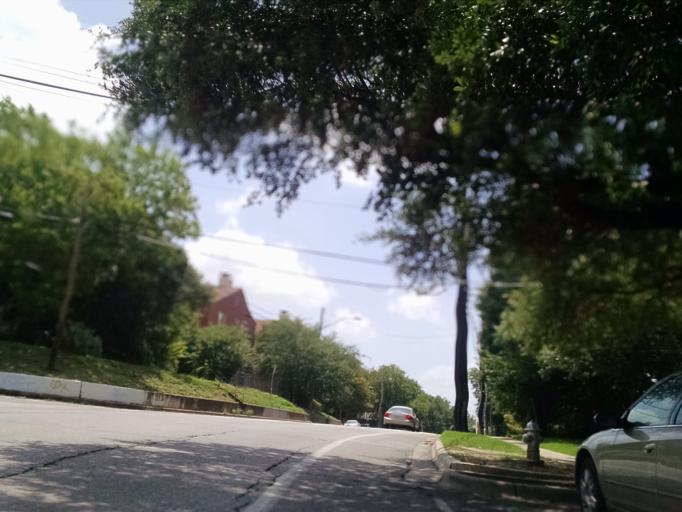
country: US
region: Texas
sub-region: Travis County
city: Austin
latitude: 30.2944
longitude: -97.7376
